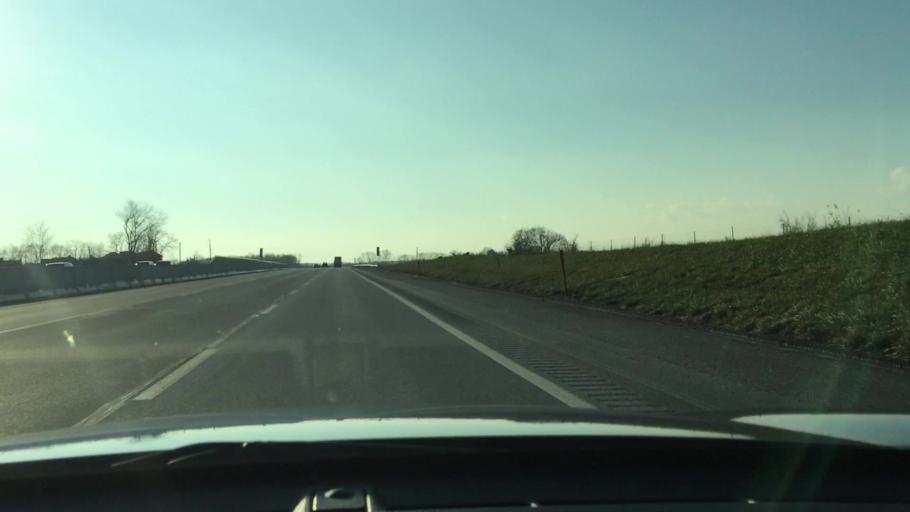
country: US
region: Pennsylvania
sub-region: Cumberland County
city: Carlisle
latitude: 40.2142
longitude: -77.2148
